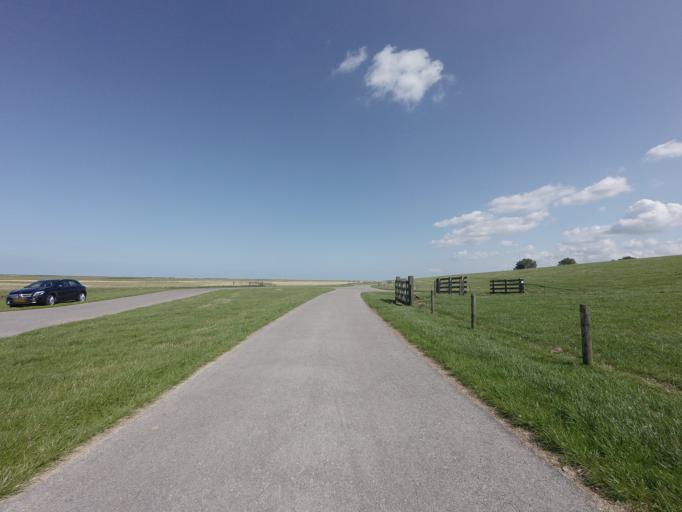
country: NL
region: Friesland
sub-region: Gemeente Ferwerderadiel
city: Marrum
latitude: 53.3410
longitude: 5.7893
